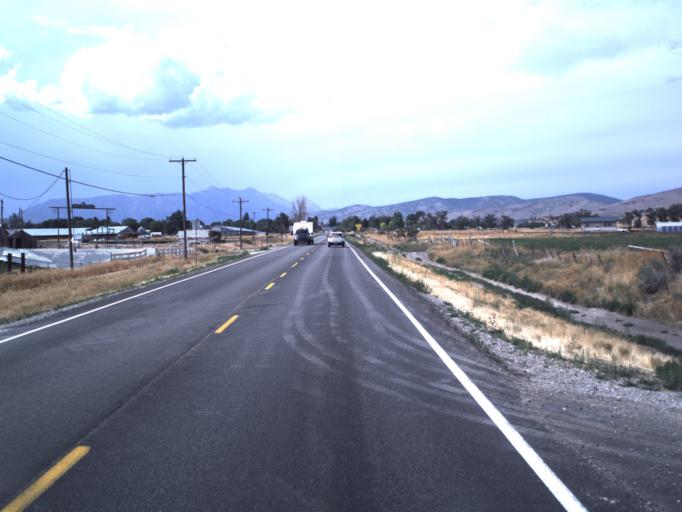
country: US
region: Utah
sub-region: Sanpete County
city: Fountain Green
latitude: 39.6143
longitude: -111.6285
